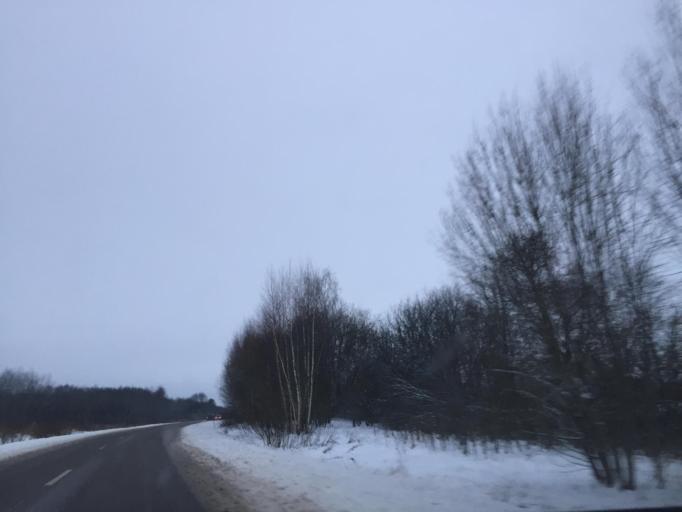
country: LV
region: Smiltene
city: Smiltene
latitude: 57.4285
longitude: 25.8545
